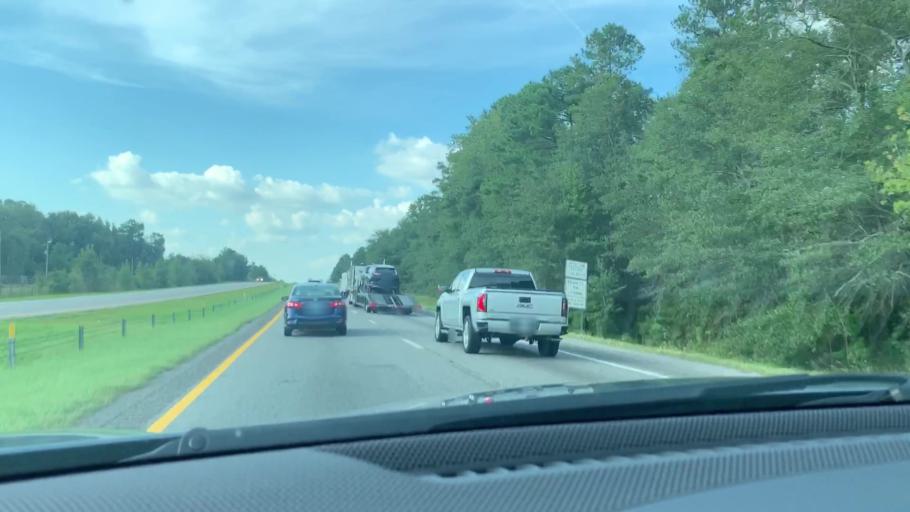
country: US
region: South Carolina
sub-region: Calhoun County
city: Saint Matthews
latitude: 33.6150
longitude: -80.8664
